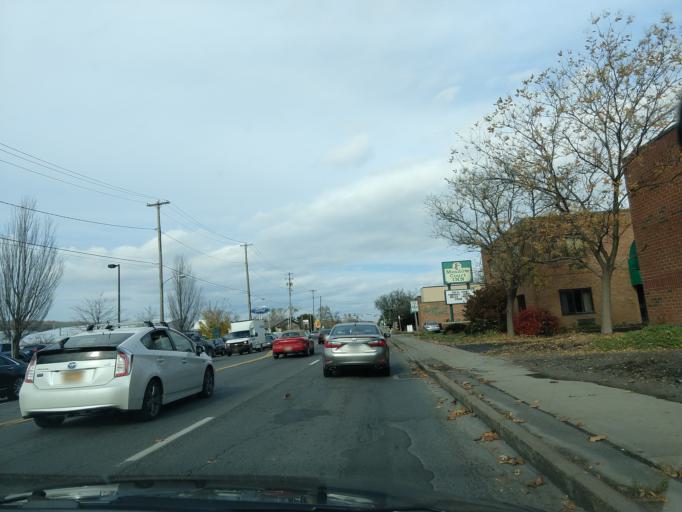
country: US
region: New York
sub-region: Tompkins County
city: Ithaca
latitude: 42.4339
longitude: -76.5081
